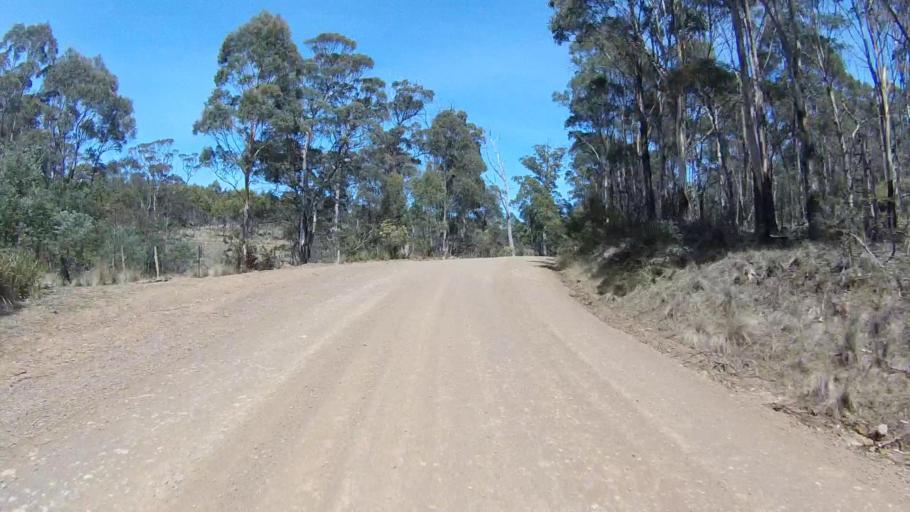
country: AU
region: Tasmania
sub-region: Sorell
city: Sorell
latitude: -42.6548
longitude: 147.7400
